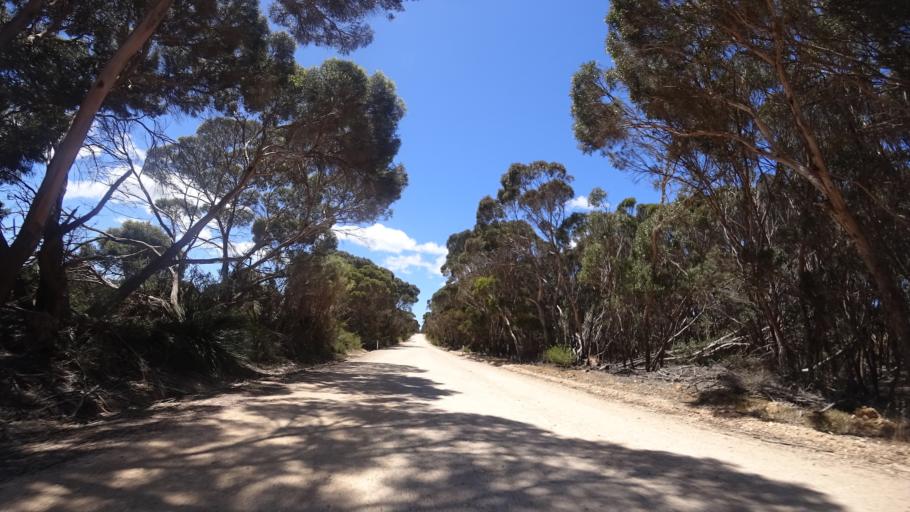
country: AU
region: South Australia
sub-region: Kangaroo Island
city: Kingscote
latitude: -35.8265
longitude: 138.0018
